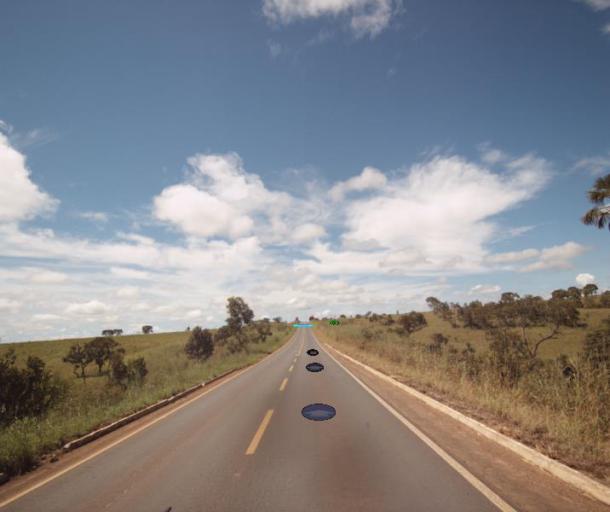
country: BR
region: Goias
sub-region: Padre Bernardo
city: Padre Bernardo
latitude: -15.2865
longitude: -48.2507
